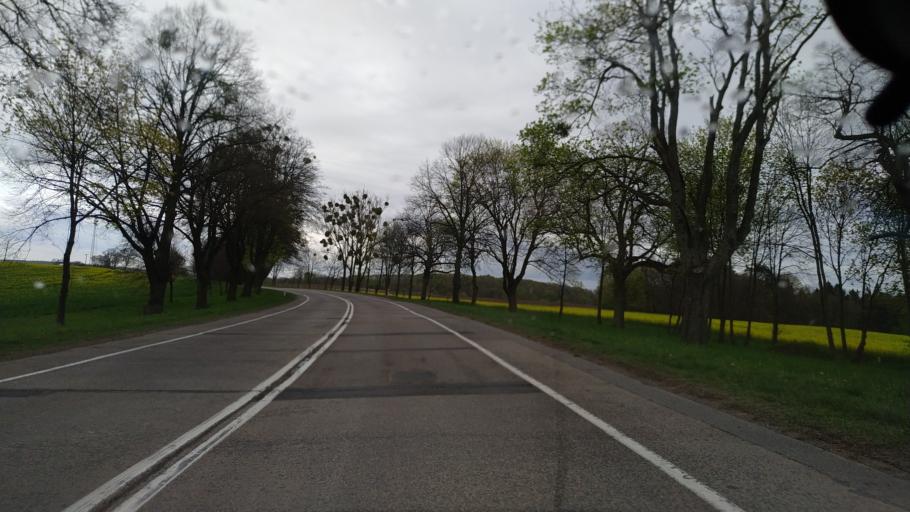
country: PL
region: Pomeranian Voivodeship
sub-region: Powiat starogardzki
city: Zblewo
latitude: 53.9318
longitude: 18.3897
